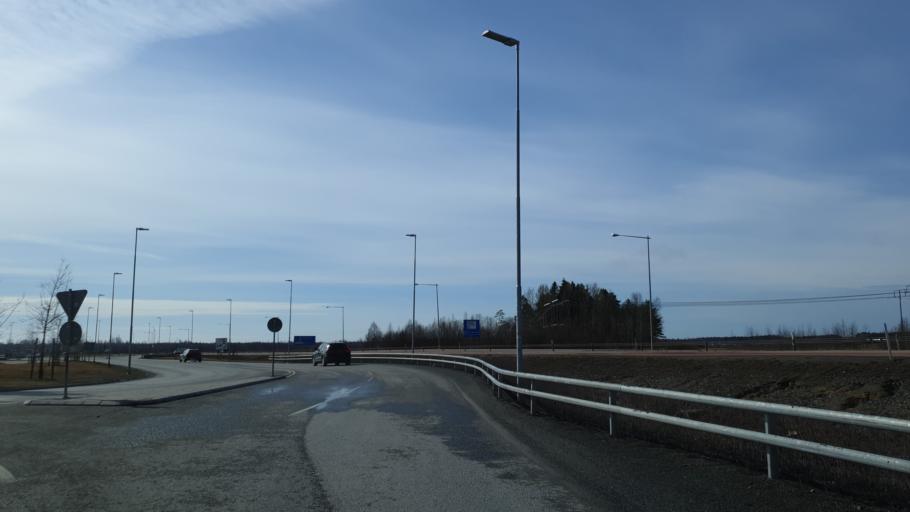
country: SE
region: Vaesterbotten
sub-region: Umea Kommun
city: Umea
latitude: 63.8089
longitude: 20.2497
